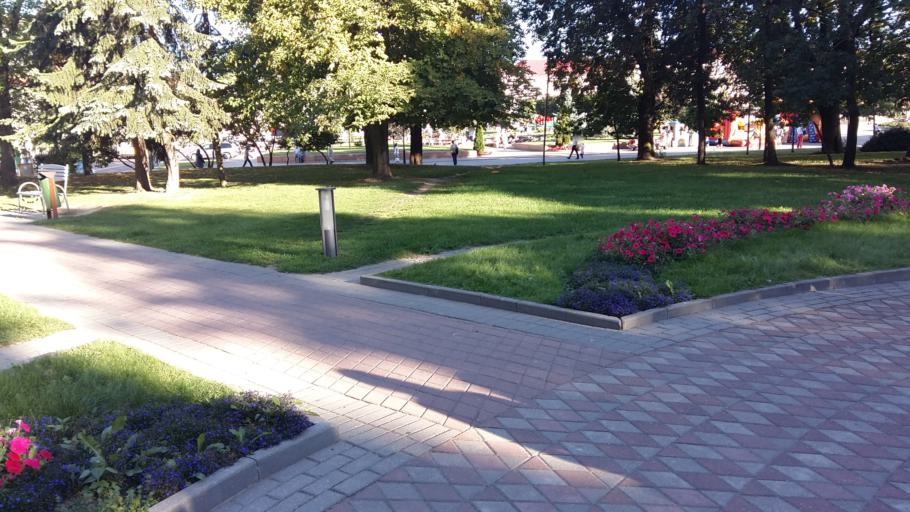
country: BY
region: Grodnenskaya
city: Hrodna
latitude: 53.6788
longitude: 23.8285
